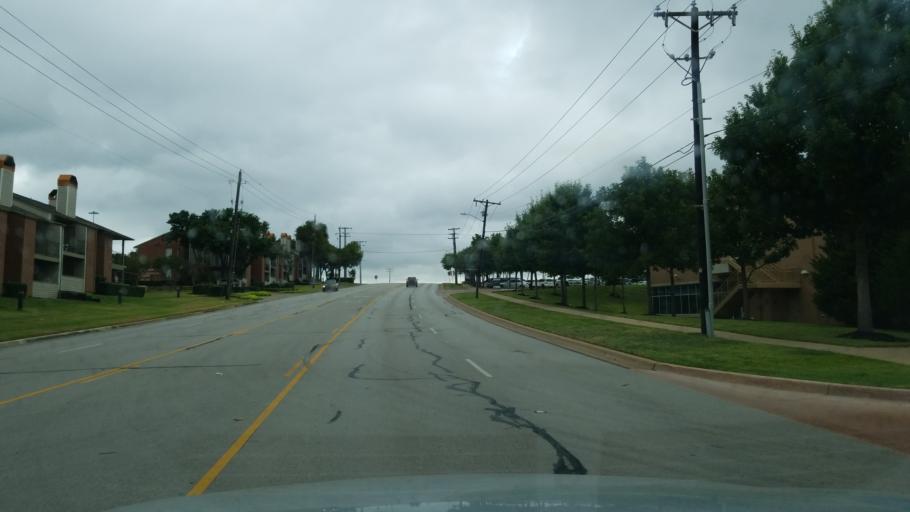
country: US
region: Texas
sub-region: Tarrant County
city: Bedford
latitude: 32.8448
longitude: -97.1126
